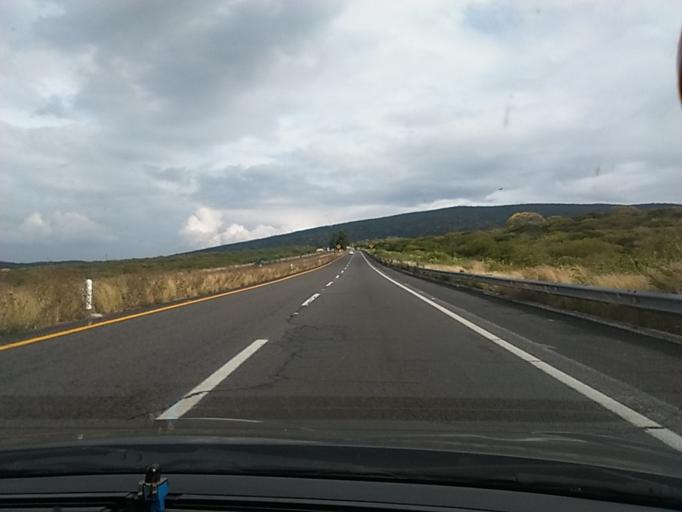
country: MX
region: Michoacan
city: Ixtlan
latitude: 20.2149
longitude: -102.3602
